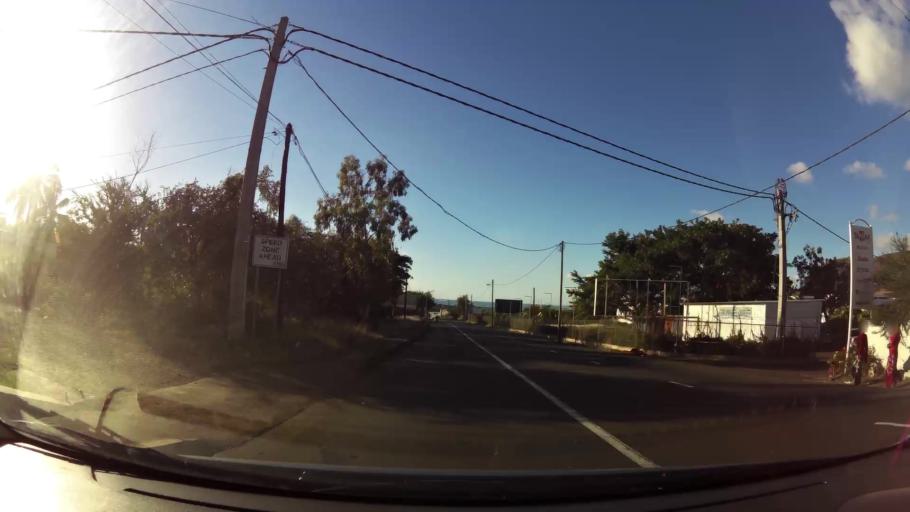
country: MU
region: Moka
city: Pailles
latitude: -20.1854
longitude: 57.4702
